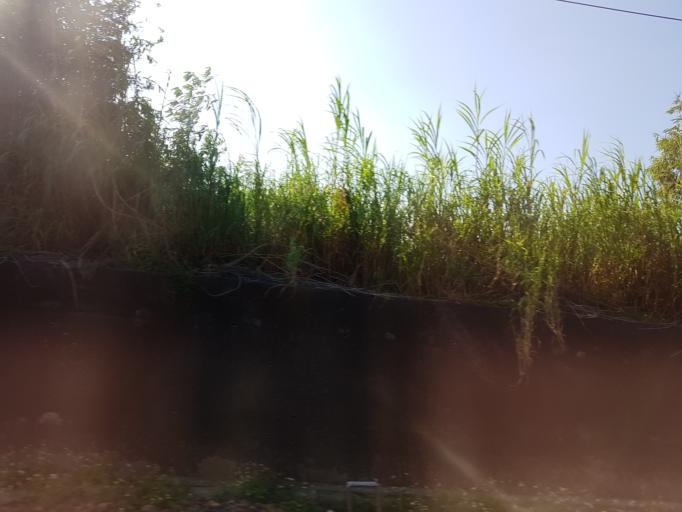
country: TW
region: Taiwan
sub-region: Miaoli
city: Miaoli
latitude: 24.5030
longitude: 120.7857
